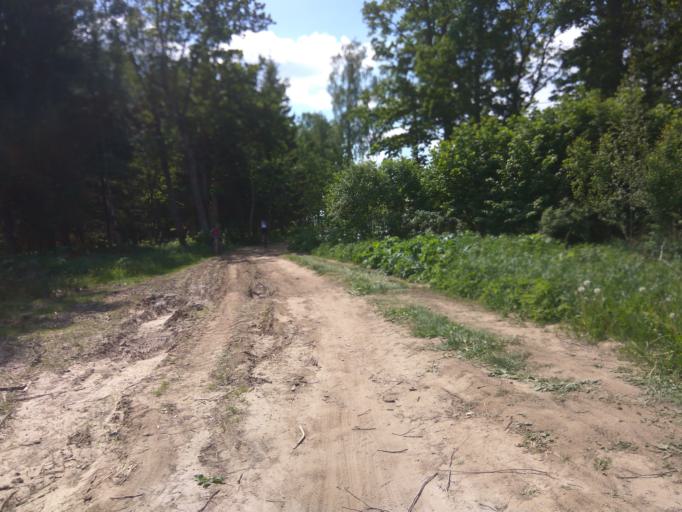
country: LV
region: Kuldigas Rajons
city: Kuldiga
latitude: 56.9324
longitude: 21.9757
